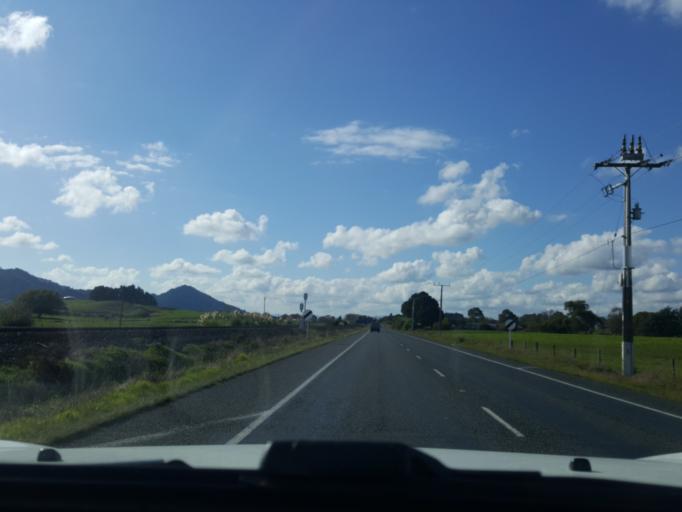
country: NZ
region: Waikato
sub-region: Waikato District
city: Ngaruawahia
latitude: -37.6503
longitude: 175.1597
